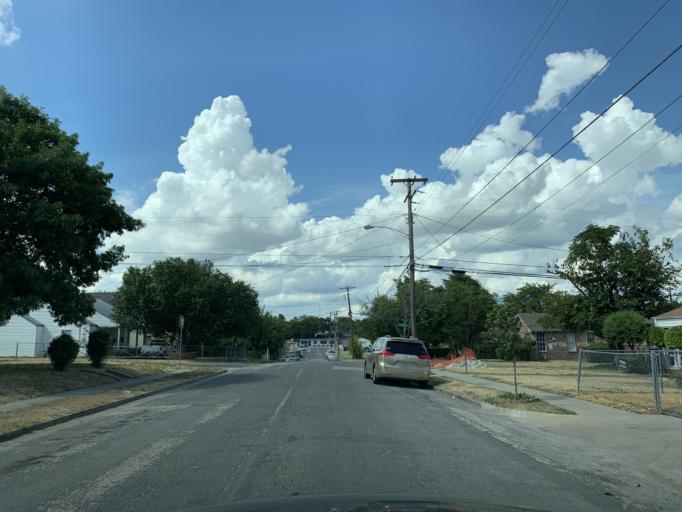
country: US
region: Texas
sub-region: Dallas County
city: Cockrell Hill
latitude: 32.7476
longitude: -96.8687
